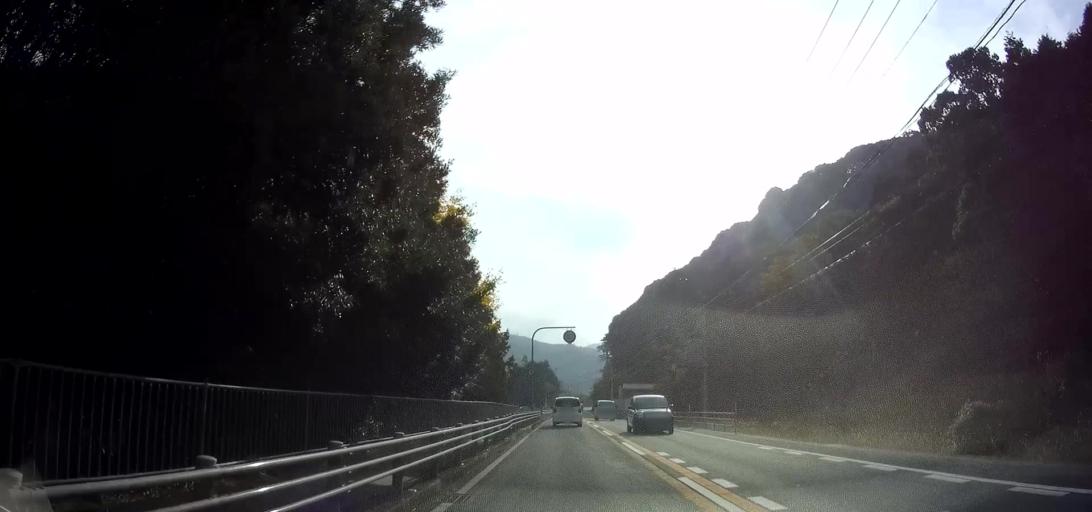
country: JP
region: Nagasaki
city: Shimabara
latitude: 32.7768
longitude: 130.2113
